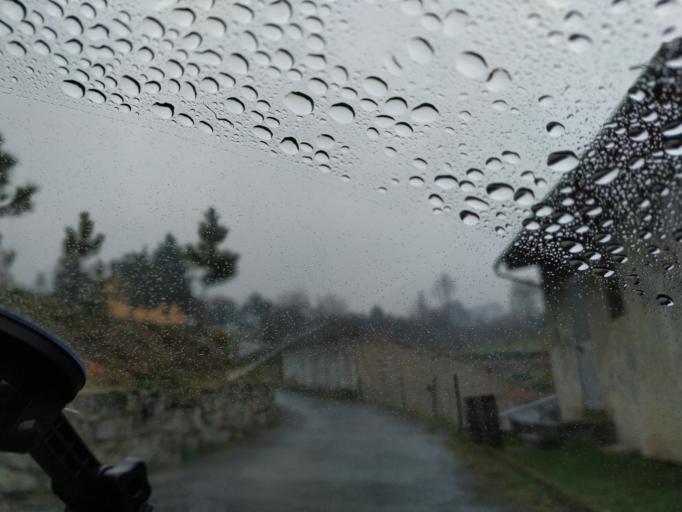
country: PT
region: Vila Real
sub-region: Vila Real
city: Vila Real
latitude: 41.3319
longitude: -7.7342
